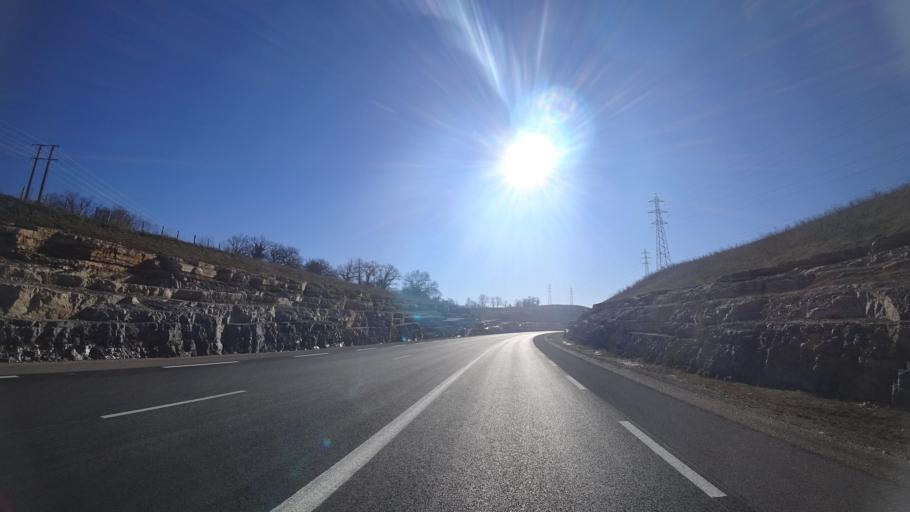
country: FR
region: Midi-Pyrenees
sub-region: Departement de l'Aveyron
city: Sebazac-Concoures
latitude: 44.3842
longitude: 2.6157
